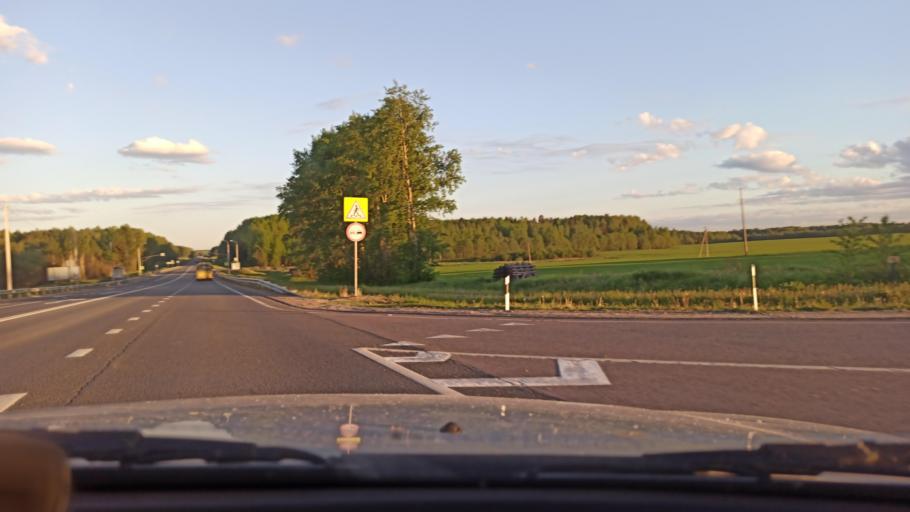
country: RU
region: Vologda
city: Molochnoye
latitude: 59.3675
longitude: 39.6717
